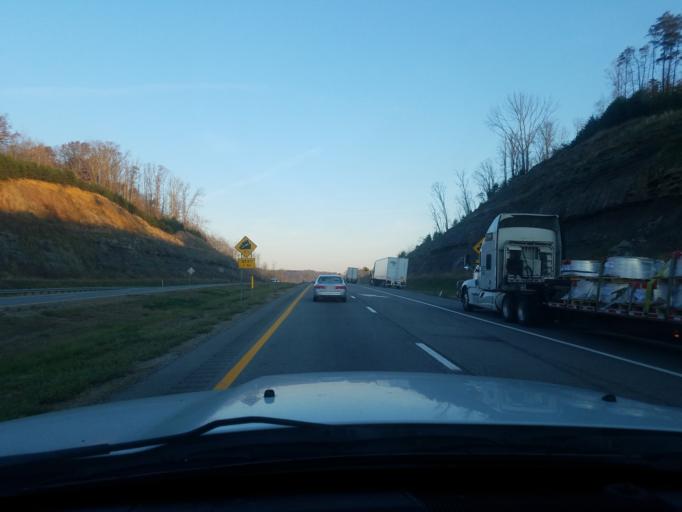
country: US
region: West Virginia
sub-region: Putnam County
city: Buffalo
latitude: 38.5728
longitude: -82.0147
